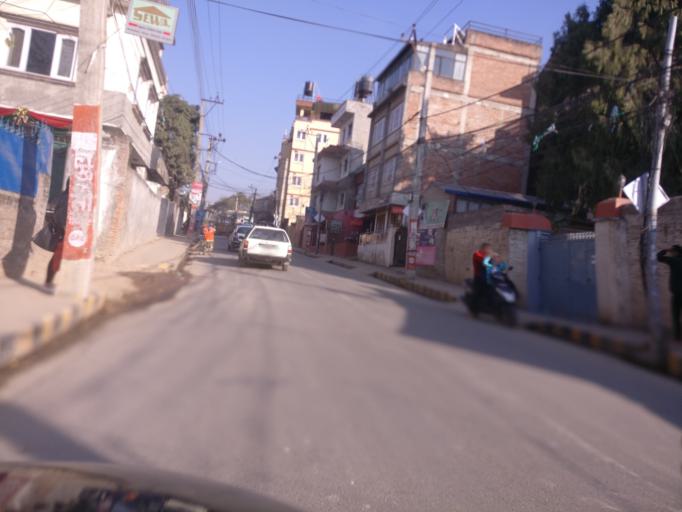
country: NP
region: Central Region
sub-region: Bagmati Zone
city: Patan
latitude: 27.6784
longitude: 85.3119
